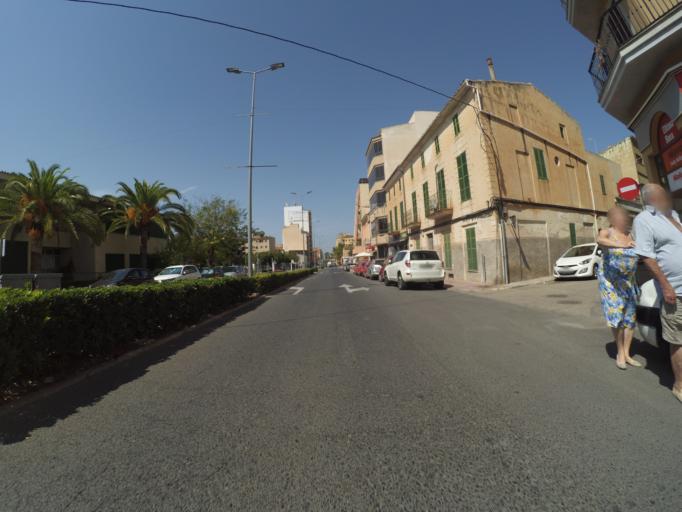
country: ES
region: Balearic Islands
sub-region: Illes Balears
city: Manacor
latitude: 39.5716
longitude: 3.2029
